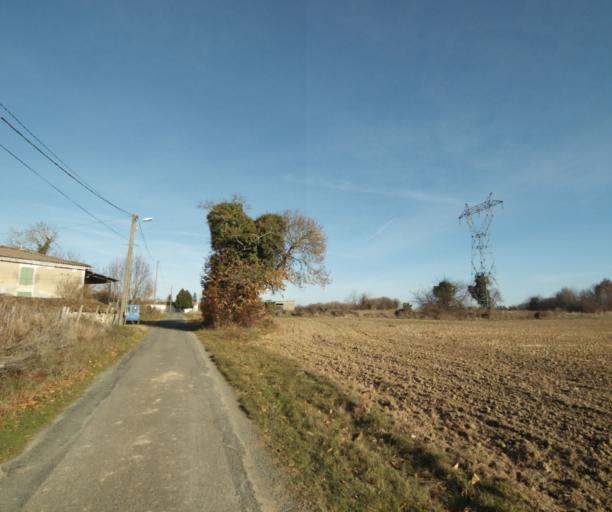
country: FR
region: Poitou-Charentes
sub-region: Departement de la Charente-Maritime
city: Cherac
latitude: 45.7412
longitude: -0.4666
